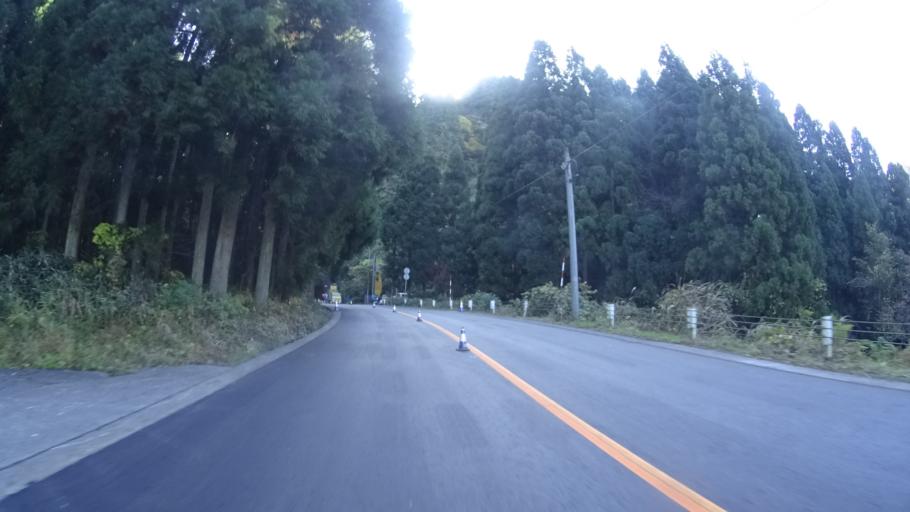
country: JP
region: Ishikawa
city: Tsurugi-asahimachi
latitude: 36.3707
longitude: 136.5829
